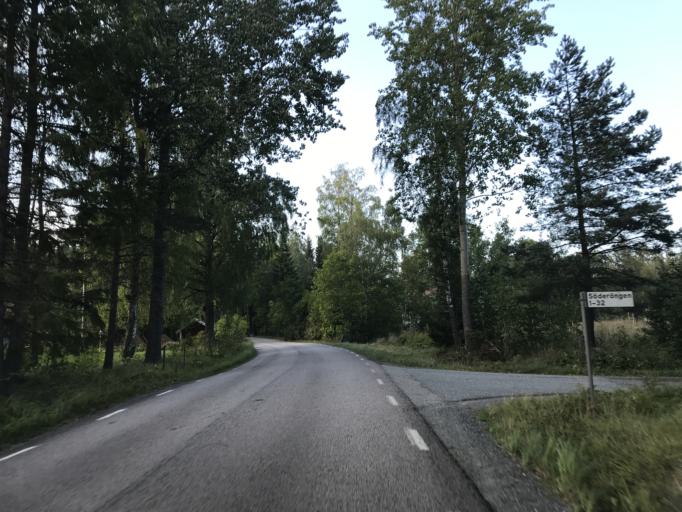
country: SE
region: Stockholm
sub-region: Norrtalje Kommun
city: Bjorko
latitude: 59.8736
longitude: 19.0130
